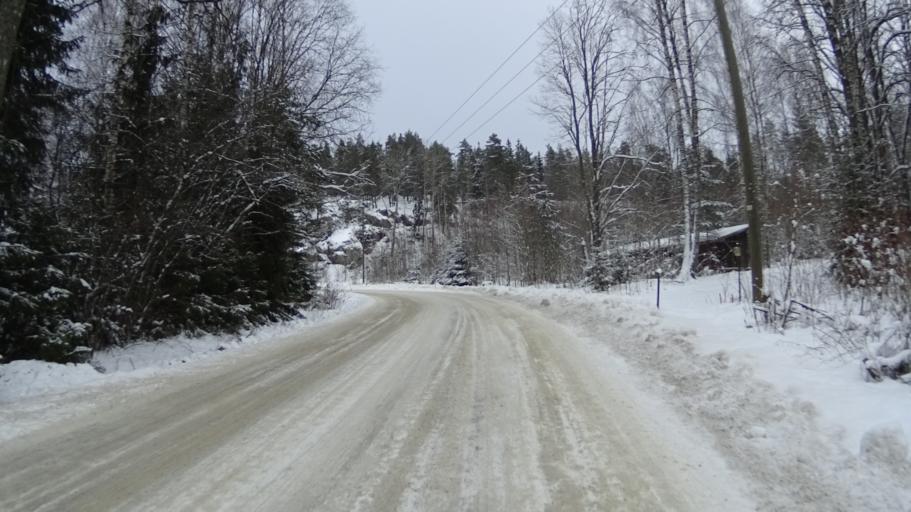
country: FI
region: Uusimaa
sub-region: Helsinki
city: Saukkola
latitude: 60.4094
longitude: 24.1130
